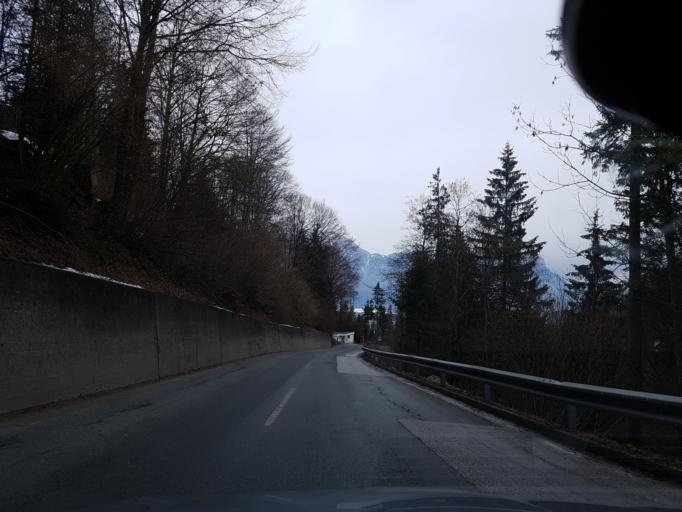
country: AT
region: Tyrol
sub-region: Politischer Bezirk Kufstein
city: Worgl
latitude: 47.4752
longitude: 12.0713
